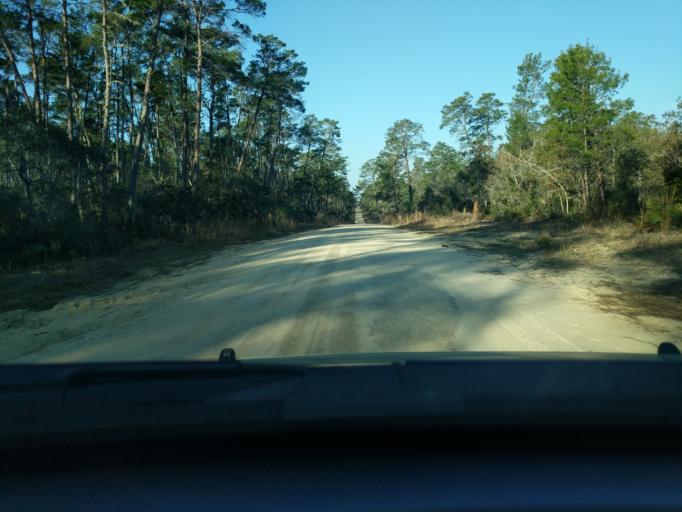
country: US
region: Florida
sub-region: Marion County
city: Silver Springs Shores
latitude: 29.2264
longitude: -81.8162
